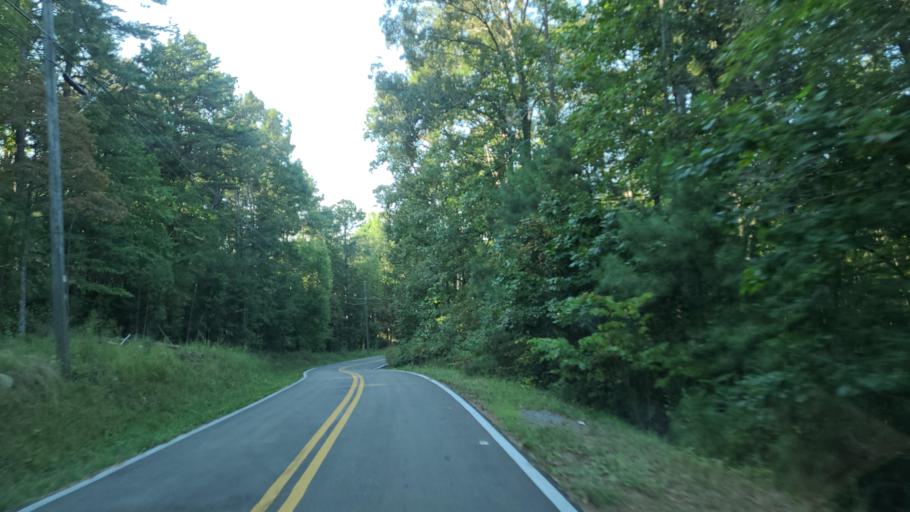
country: US
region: Georgia
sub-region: Pickens County
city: Nelson
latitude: 34.4065
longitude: -84.4143
